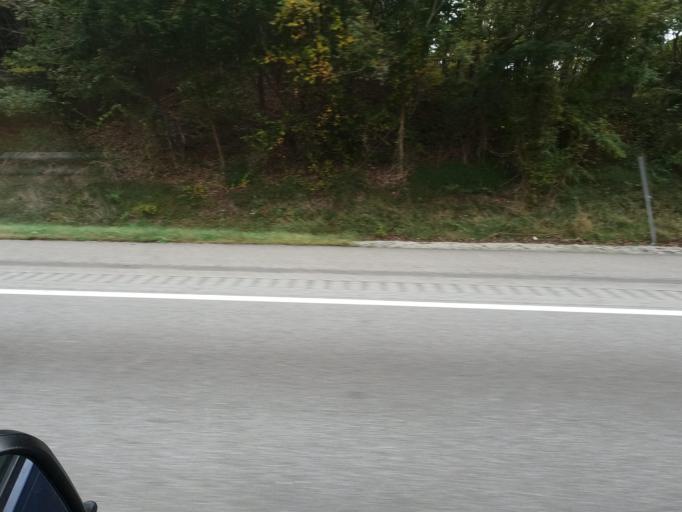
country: US
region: Tennessee
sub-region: Dickson County
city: Dickson
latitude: 35.9972
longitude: -87.4626
